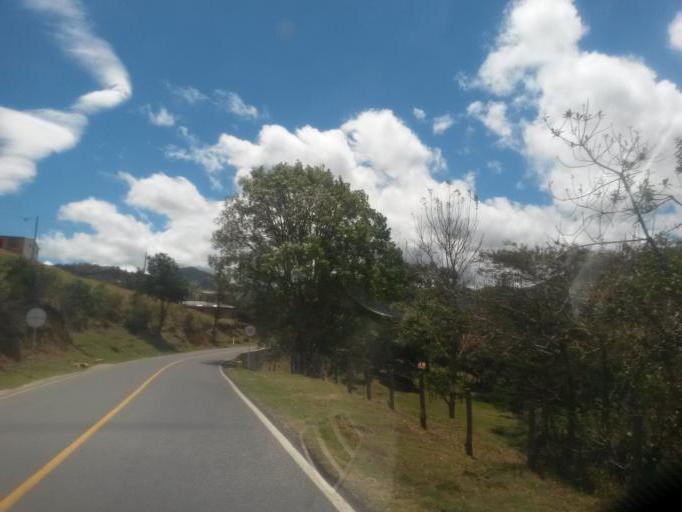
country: CO
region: Cauca
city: Silvia
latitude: 2.6072
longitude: -76.3880
